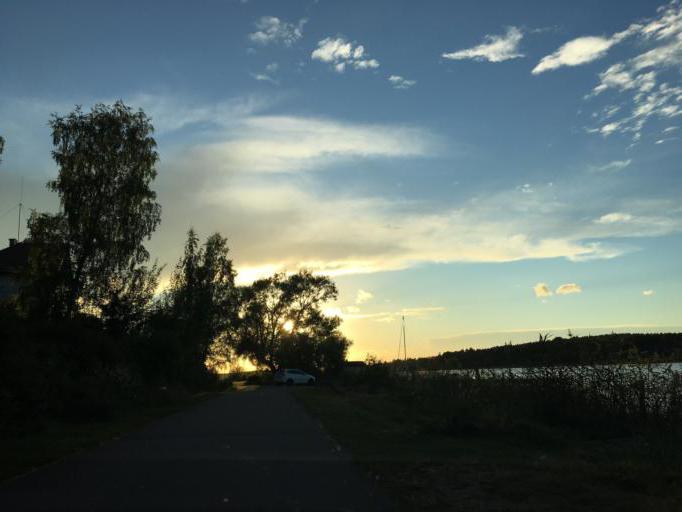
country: SE
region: Soedermanland
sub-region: Eskilstuna Kommun
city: Torshalla
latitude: 59.4365
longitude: 16.4530
